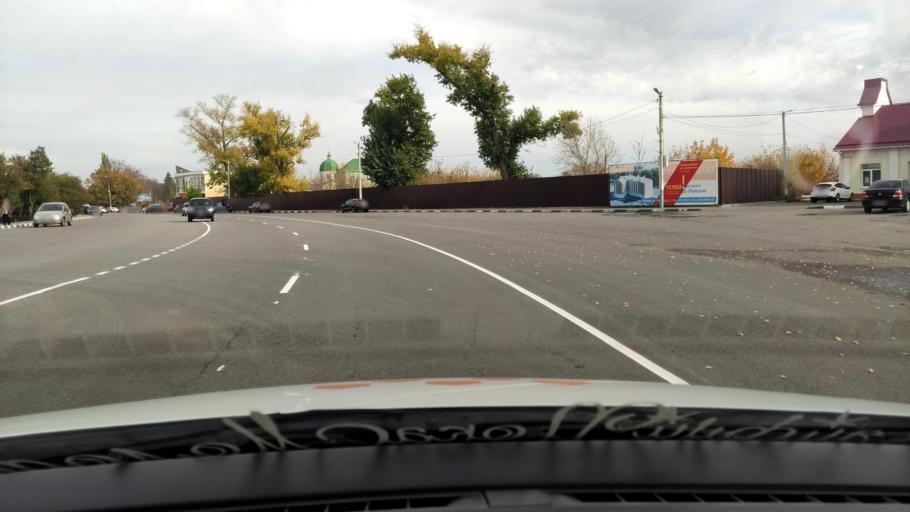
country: RU
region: Voronezj
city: Ramon'
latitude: 51.9103
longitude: 39.3380
